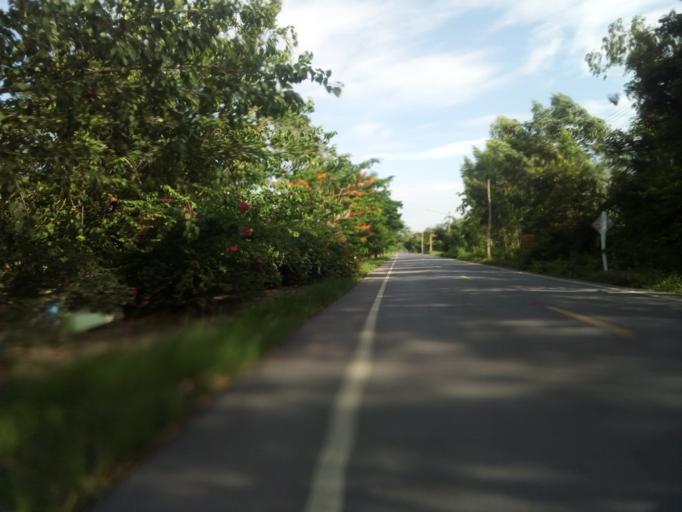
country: TH
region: Pathum Thani
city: Nong Suea
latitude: 14.1139
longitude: 100.8461
